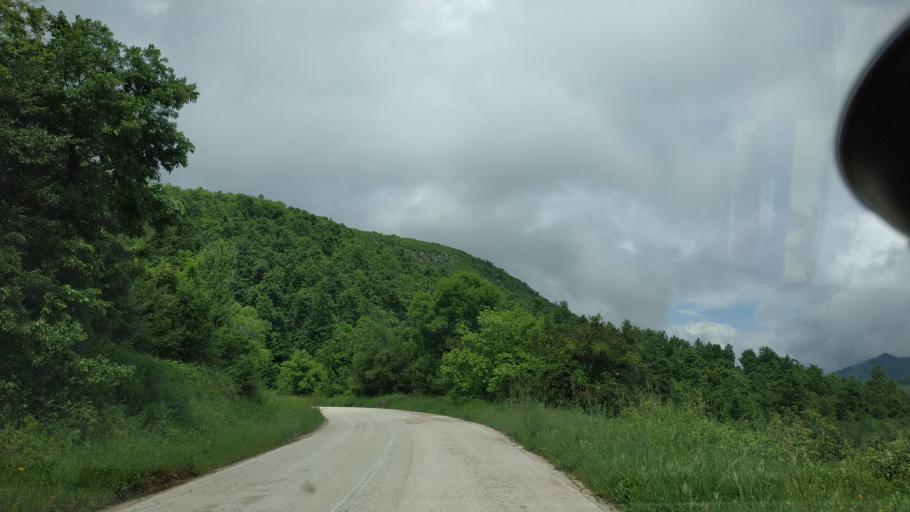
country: RS
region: Central Serbia
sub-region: Zajecarski Okrug
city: Boljevac
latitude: 43.7362
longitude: 21.9521
